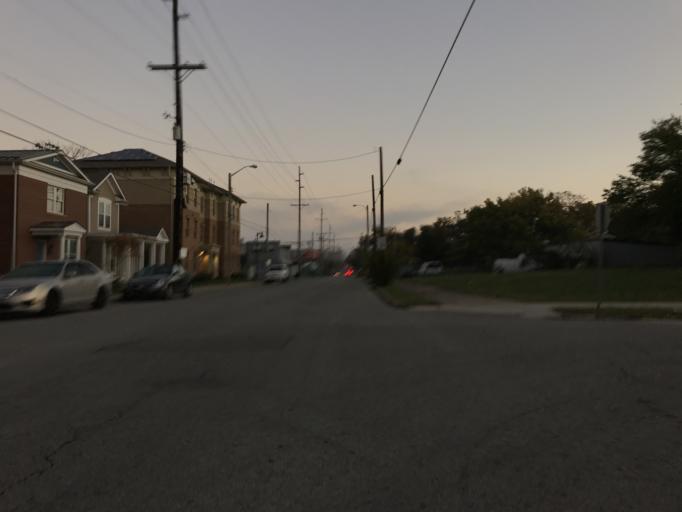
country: US
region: Kentucky
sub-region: Jefferson County
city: Louisville
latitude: 38.2422
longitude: -85.7420
